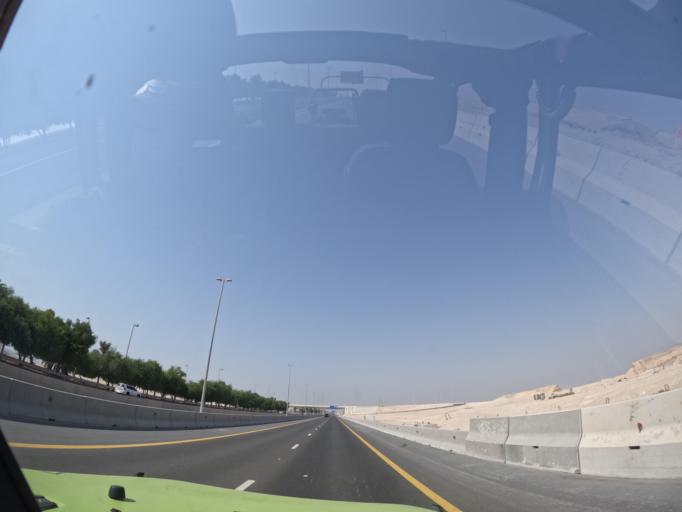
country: AE
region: Abu Dhabi
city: Abu Dhabi
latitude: 24.4270
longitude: 54.6782
